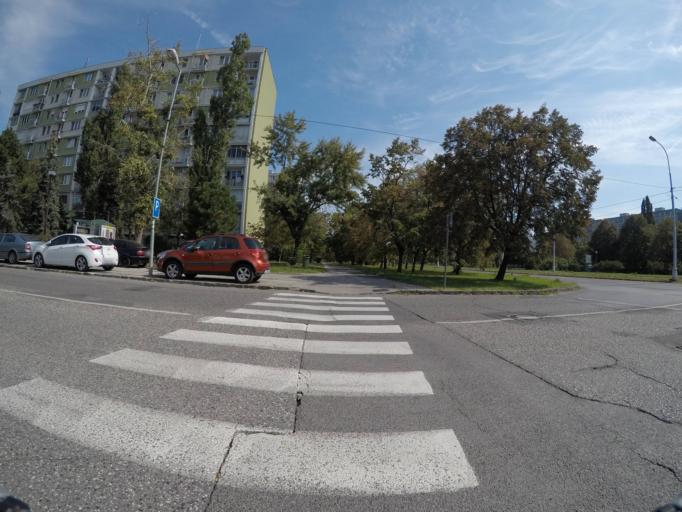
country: SK
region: Bratislavsky
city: Bratislava
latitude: 48.1573
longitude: 17.1565
